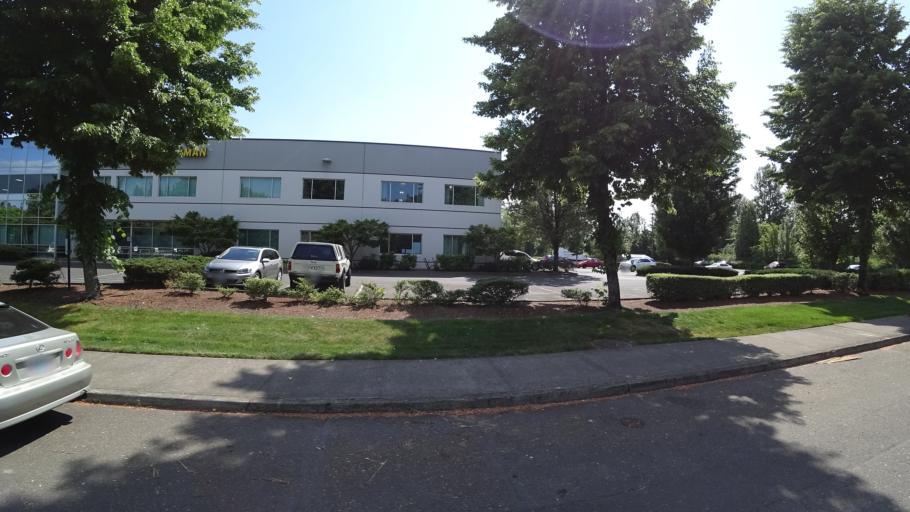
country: US
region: Oregon
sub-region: Multnomah County
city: Lents
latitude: 45.5652
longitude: -122.5393
